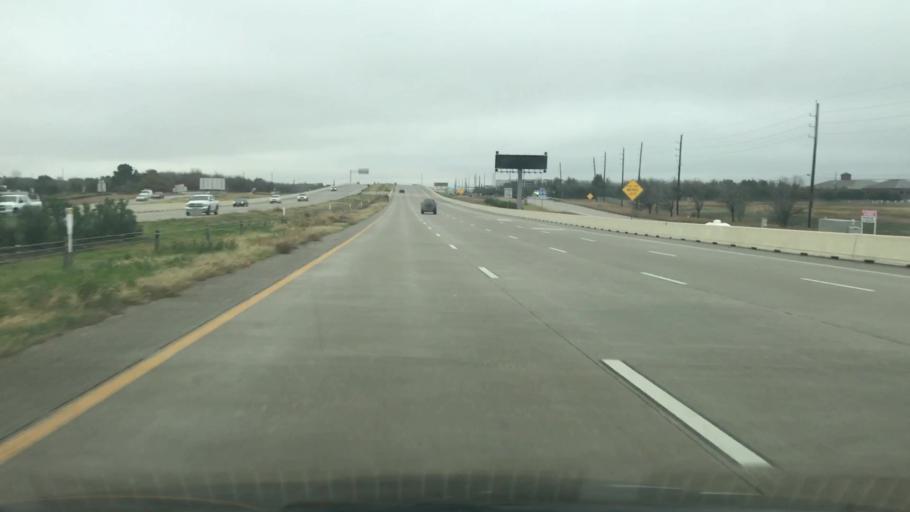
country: US
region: Texas
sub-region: Harris County
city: Katy
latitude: 29.7964
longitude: -95.7761
